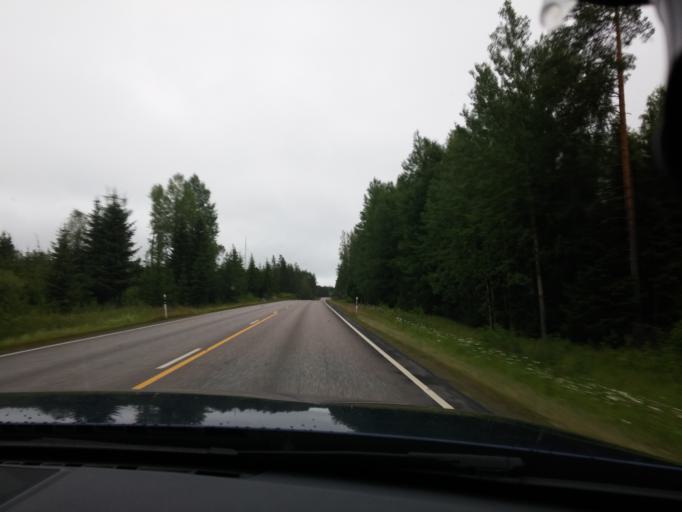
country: FI
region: Pirkanmaa
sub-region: Ylae-Pirkanmaa
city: Vilppula
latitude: 61.9172
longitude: 24.5333
